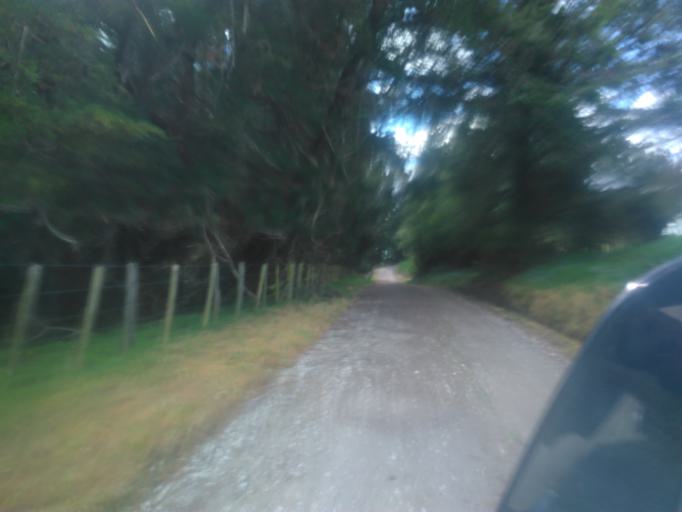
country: NZ
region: Hawke's Bay
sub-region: Wairoa District
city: Wairoa
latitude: -38.7739
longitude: 177.6375
